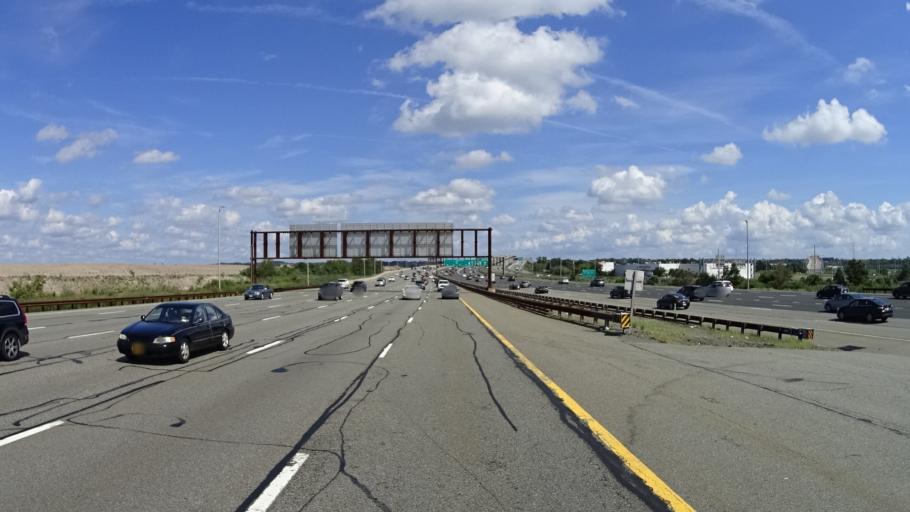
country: US
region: New Jersey
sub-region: Middlesex County
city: South Amboy
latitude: 40.4970
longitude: -74.3008
